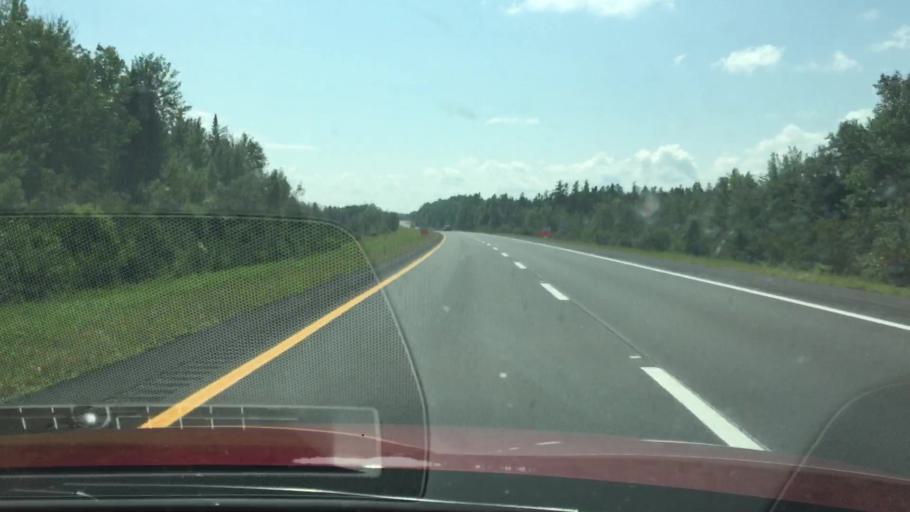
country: US
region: Maine
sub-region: Penobscot County
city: Patten
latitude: 45.8864
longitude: -68.4069
